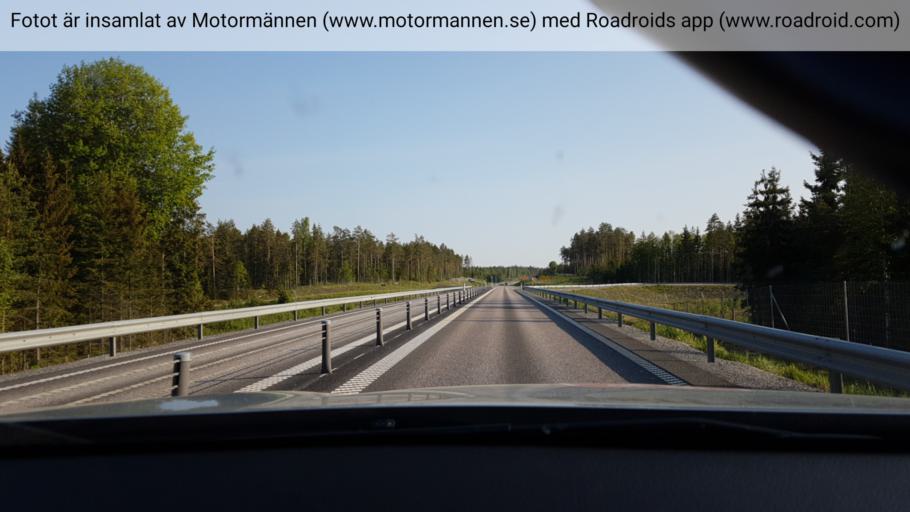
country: SE
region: Uppsala
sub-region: Heby Kommun
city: Tarnsjo
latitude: 60.0934
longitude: 16.9188
